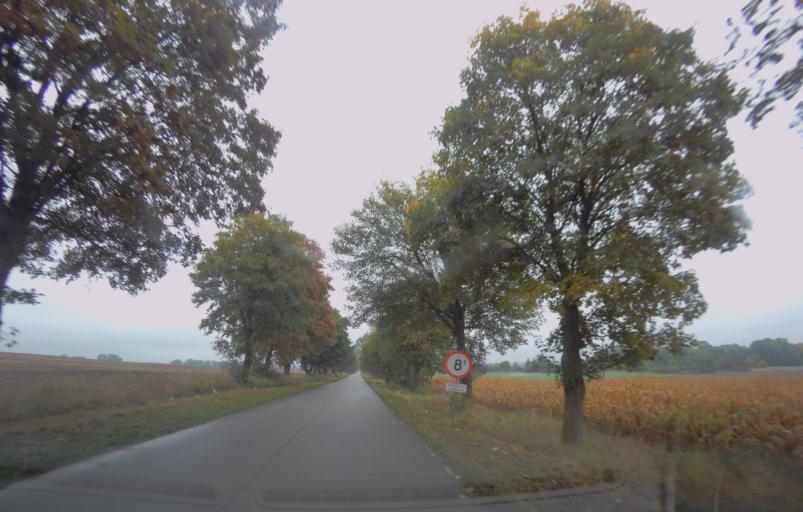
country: PL
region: Lublin Voivodeship
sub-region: Powiat chelmski
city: Sawin
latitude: 51.2139
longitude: 23.4410
